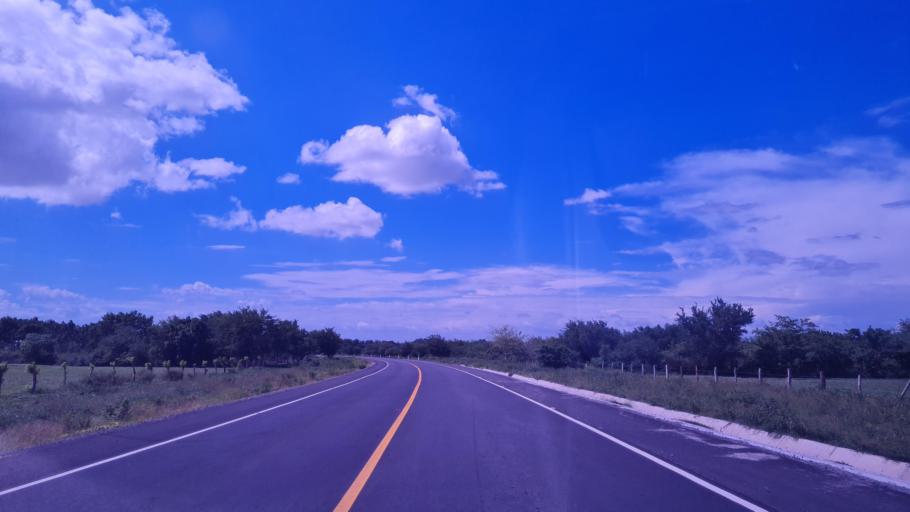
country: NI
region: Managua
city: Managua
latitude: 12.1132
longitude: -86.1522
